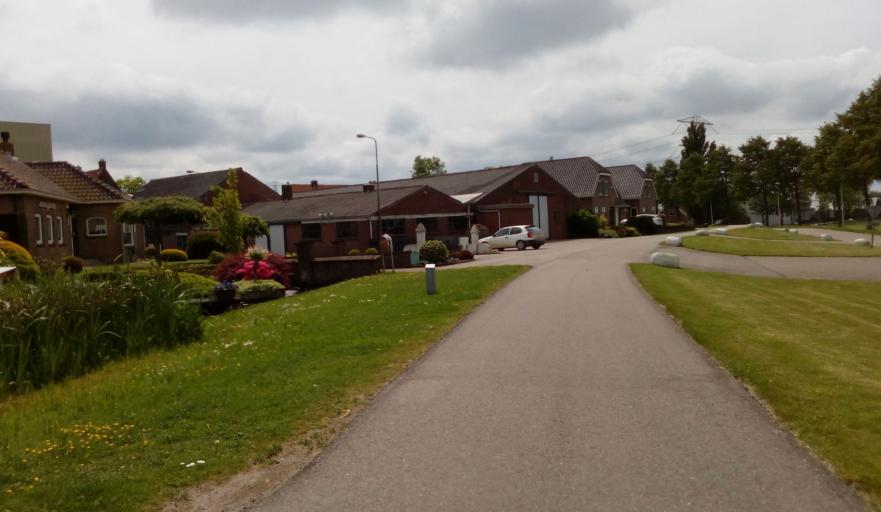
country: NL
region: South Holland
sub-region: Gemeente Lansingerland
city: Bleiswijk
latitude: 52.0146
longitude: 4.5786
